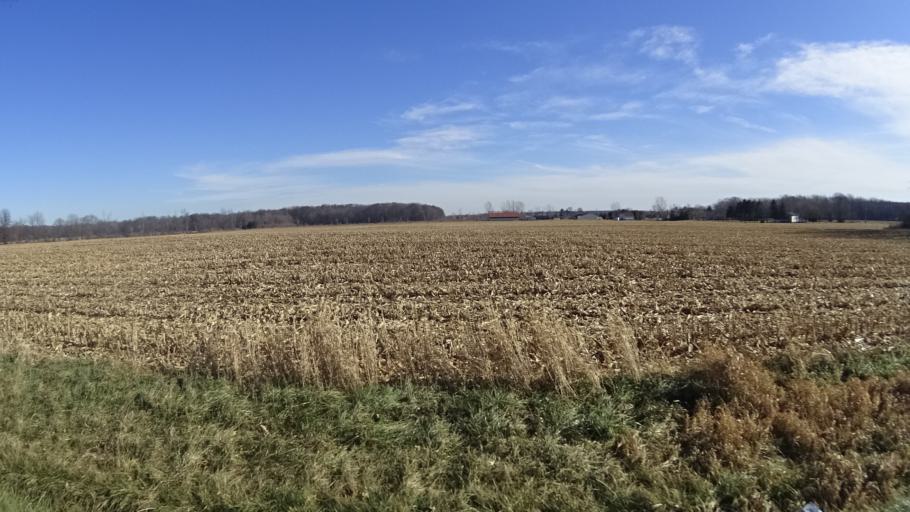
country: US
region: Ohio
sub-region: Lorain County
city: Camden
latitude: 41.2895
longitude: -82.3013
